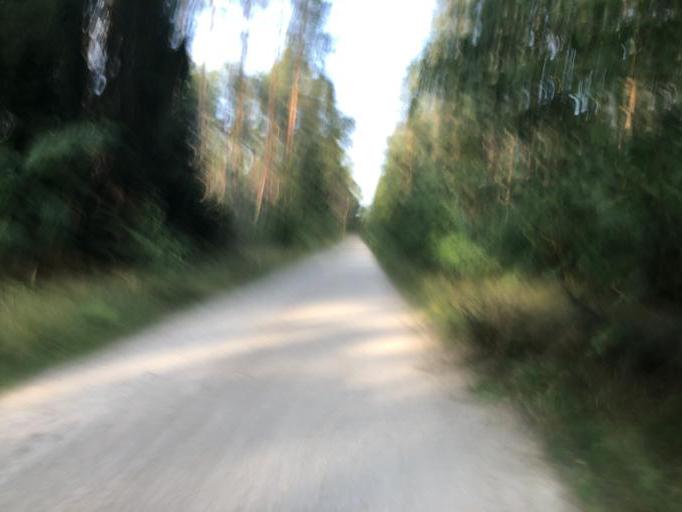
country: DE
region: Bavaria
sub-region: Regierungsbezirk Mittelfranken
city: Uttenreuth
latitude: 49.5713
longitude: 11.0948
